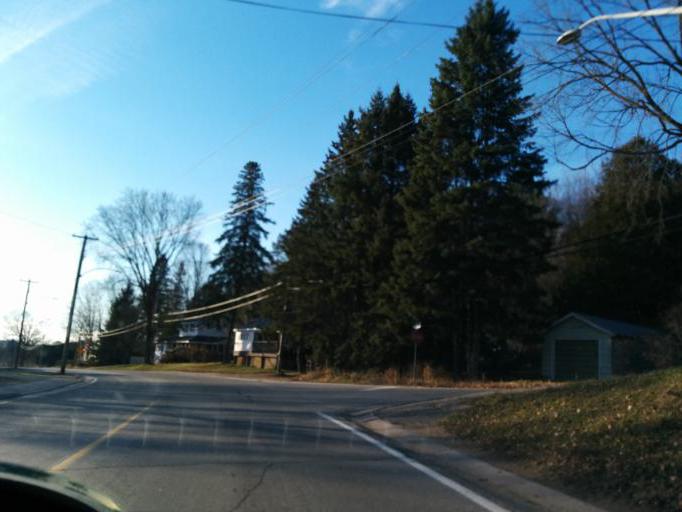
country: CA
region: Ontario
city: Bancroft
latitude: 45.0502
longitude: -78.5110
